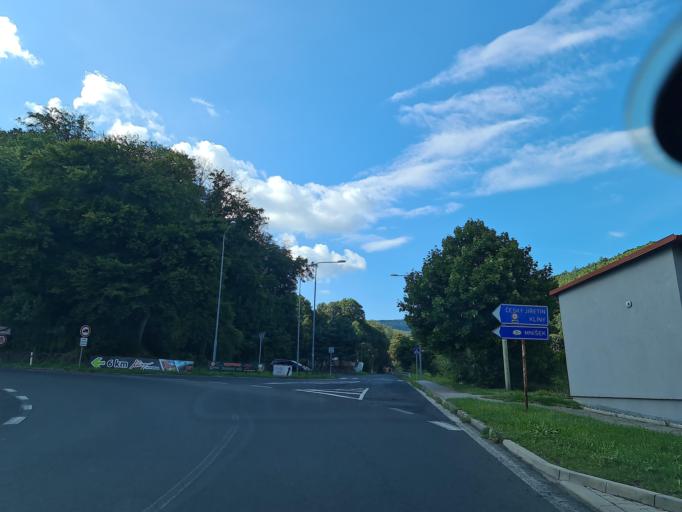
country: CZ
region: Ustecky
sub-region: Okres Most
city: Litvinov
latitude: 50.6004
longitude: 13.6005
